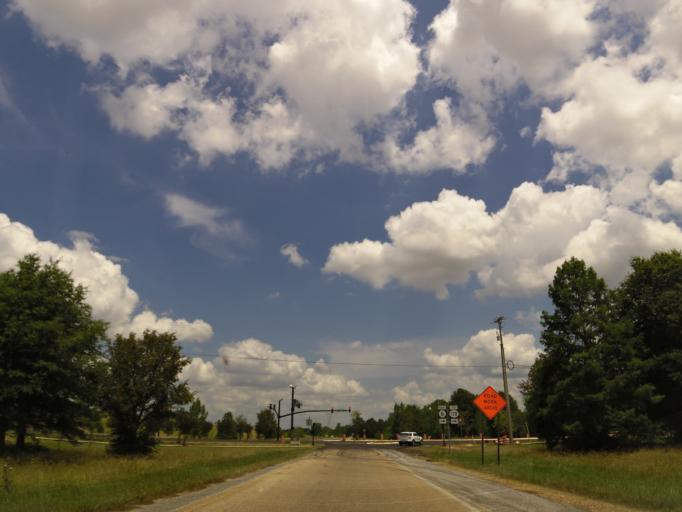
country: US
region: Mississippi
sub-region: Lee County
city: Tupelo
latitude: 34.2568
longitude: -88.6926
